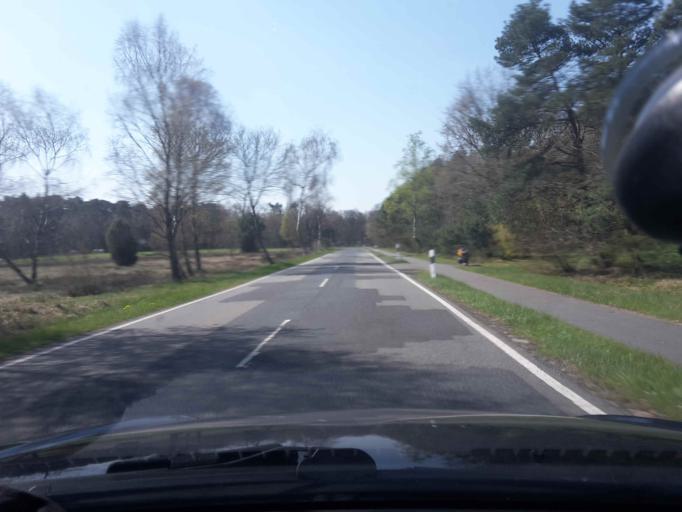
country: DE
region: Lower Saxony
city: Handeloh
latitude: 53.2412
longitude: 9.8676
